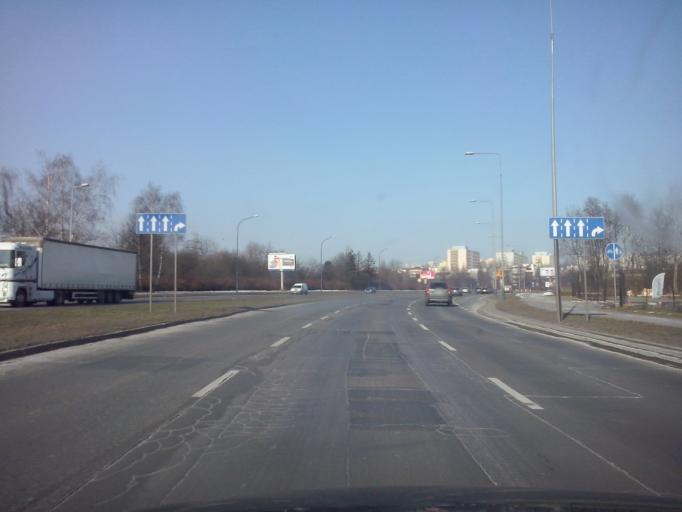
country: PL
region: Lesser Poland Voivodeship
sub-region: Krakow
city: Krakow
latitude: 50.0796
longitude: 19.9997
